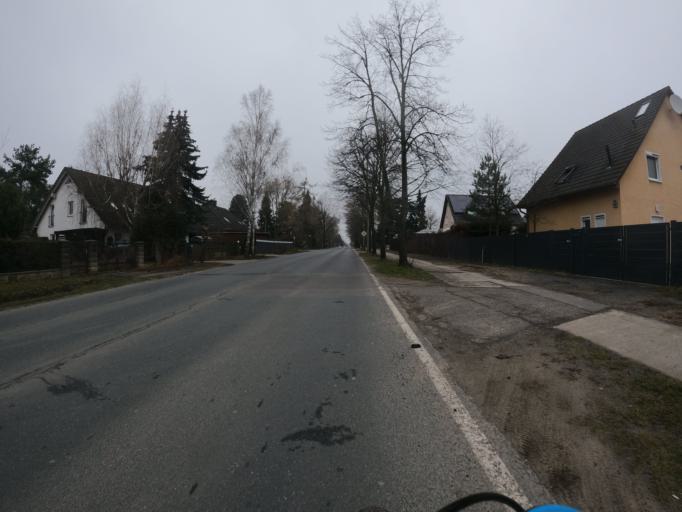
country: DE
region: Brandenburg
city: Hoppegarten
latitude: 52.5311
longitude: 13.6425
